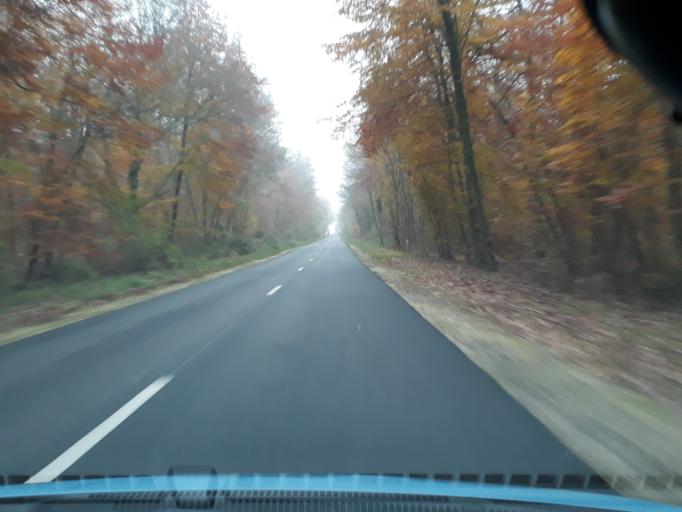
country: FR
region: Ile-de-France
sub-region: Departement de Seine-et-Marne
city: Thomery
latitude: 48.3902
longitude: 2.7742
